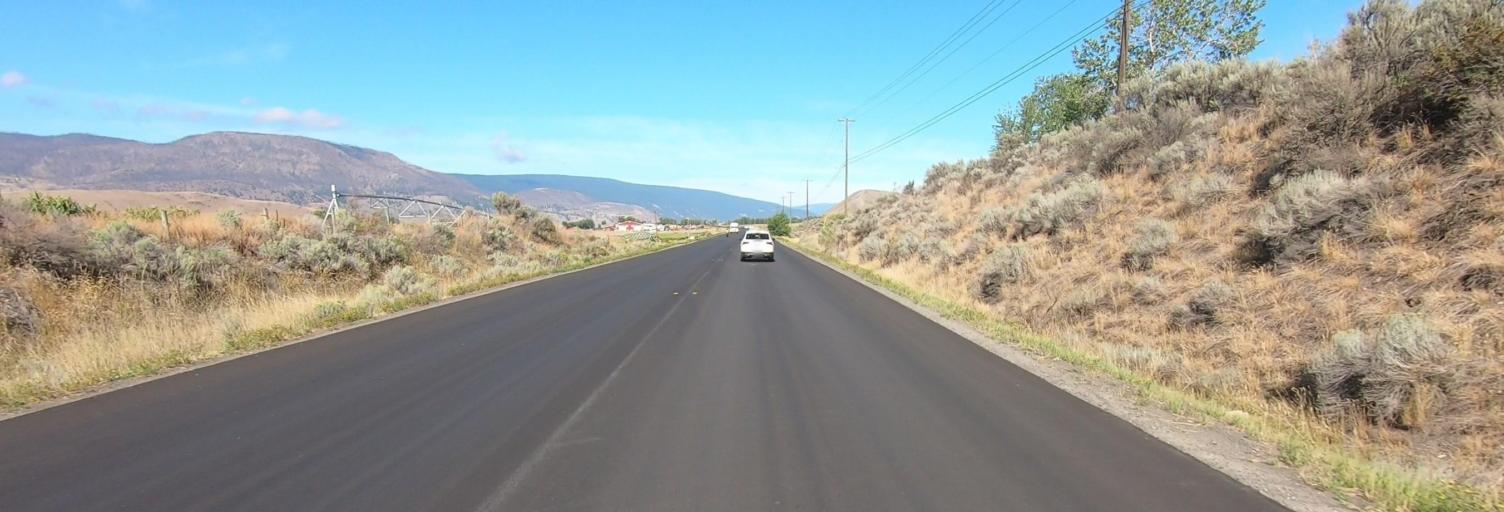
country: CA
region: British Columbia
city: Cache Creek
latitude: 50.8002
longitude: -121.2645
